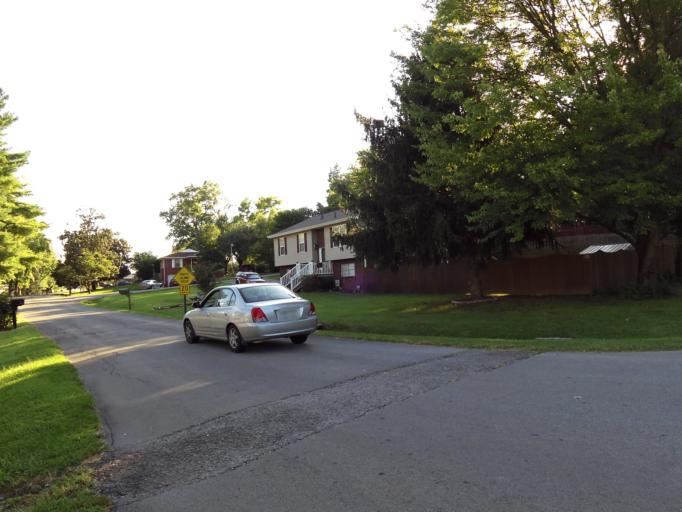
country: US
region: Tennessee
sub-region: Blount County
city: Eagleton Village
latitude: 35.8007
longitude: -83.9466
